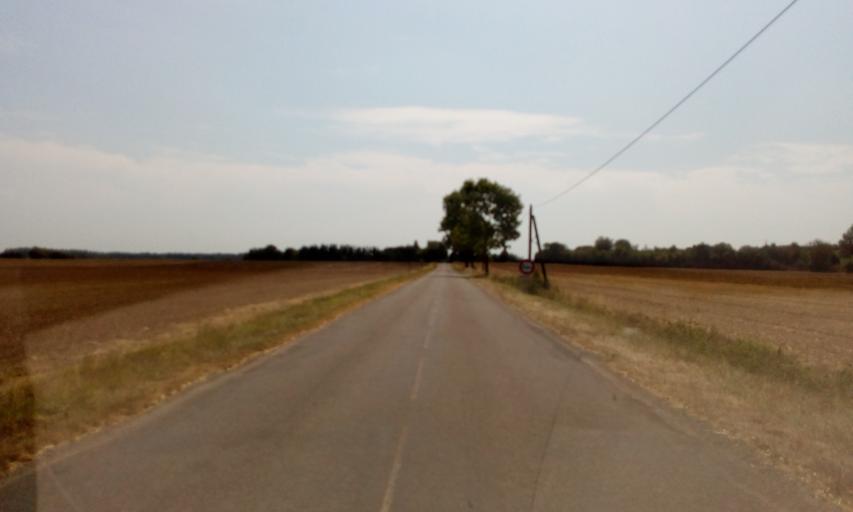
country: FR
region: Lorraine
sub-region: Departement de la Meuse
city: Verdun
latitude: 49.2094
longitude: 5.4859
